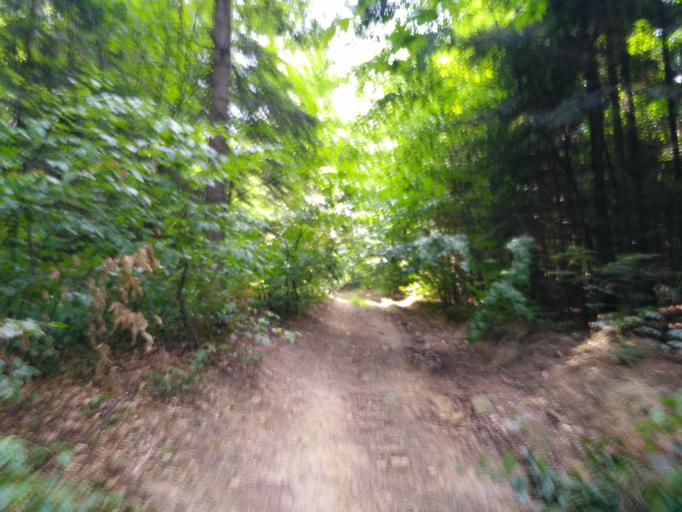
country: PL
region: Subcarpathian Voivodeship
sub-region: Powiat strzyzowski
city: Frysztak
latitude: 49.8879
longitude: 21.5469
